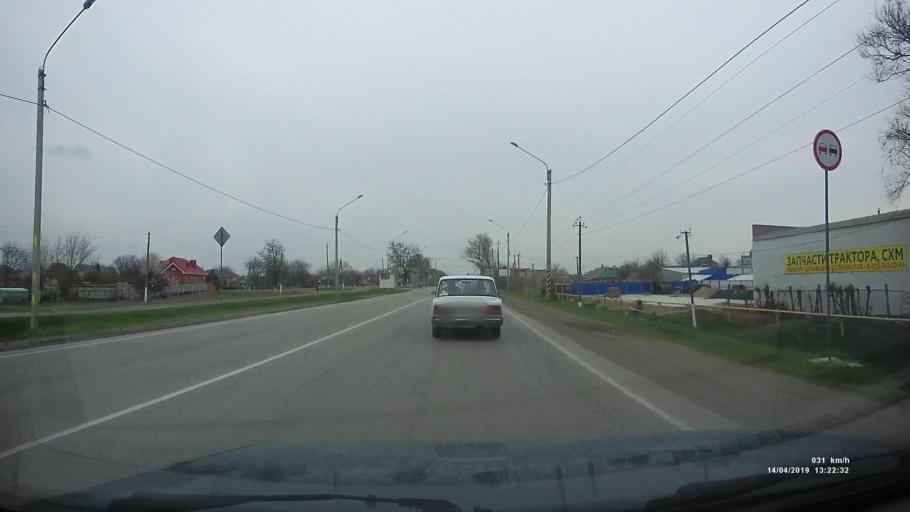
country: RU
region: Rostov
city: Kuleshovka
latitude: 47.0831
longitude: 39.5095
